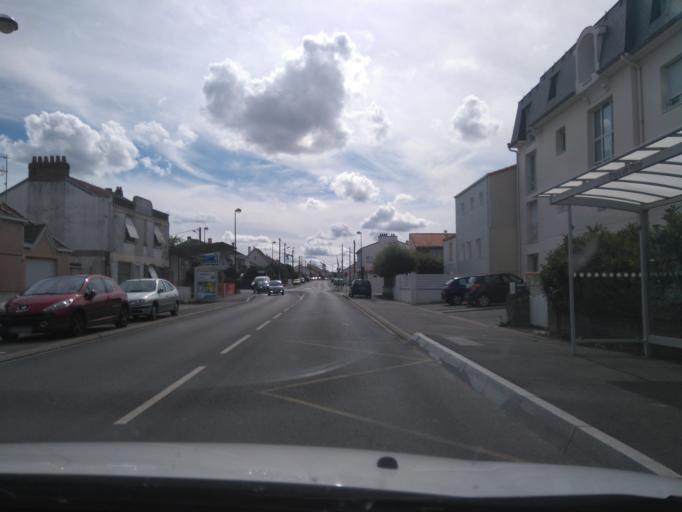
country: FR
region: Pays de la Loire
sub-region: Departement de la Loire-Atlantique
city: Reze
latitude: 47.1795
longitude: -1.5589
